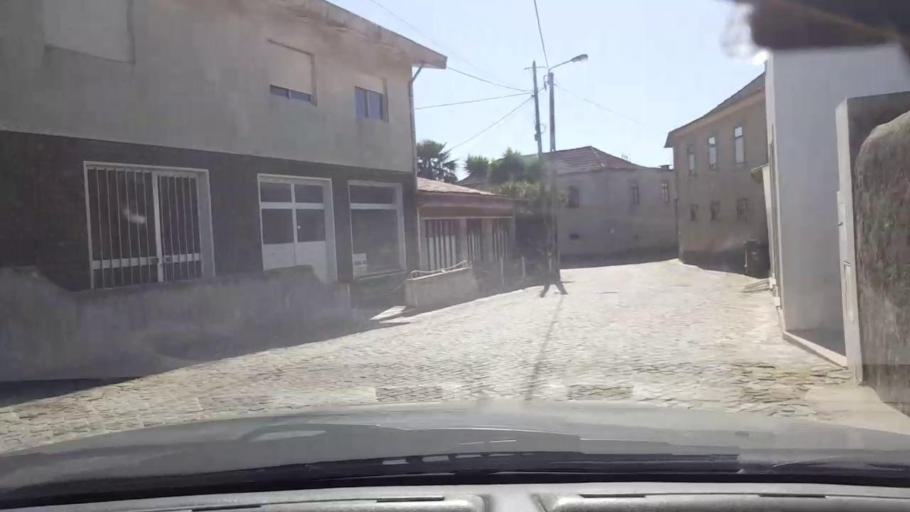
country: PT
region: Porto
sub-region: Matosinhos
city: Lavra
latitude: 41.2950
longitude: -8.7245
